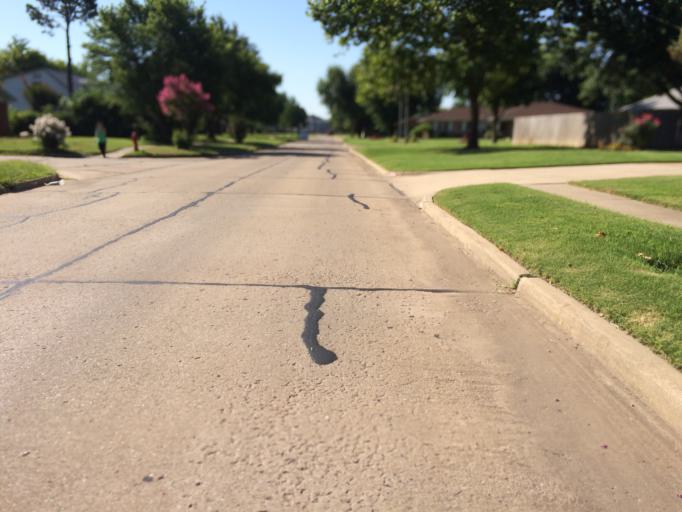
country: US
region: Oklahoma
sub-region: Cleveland County
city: Norman
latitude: 35.2300
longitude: -97.4631
